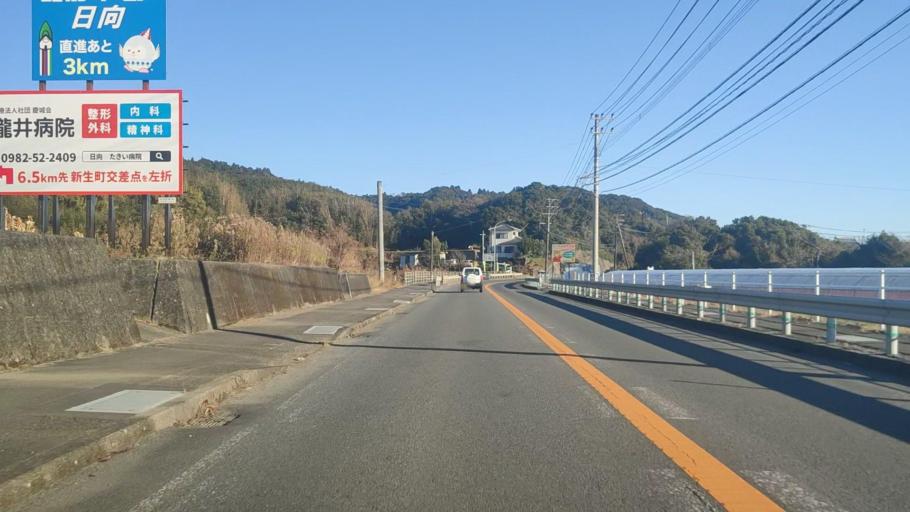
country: JP
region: Miyazaki
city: Nobeoka
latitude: 32.3633
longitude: 131.6232
